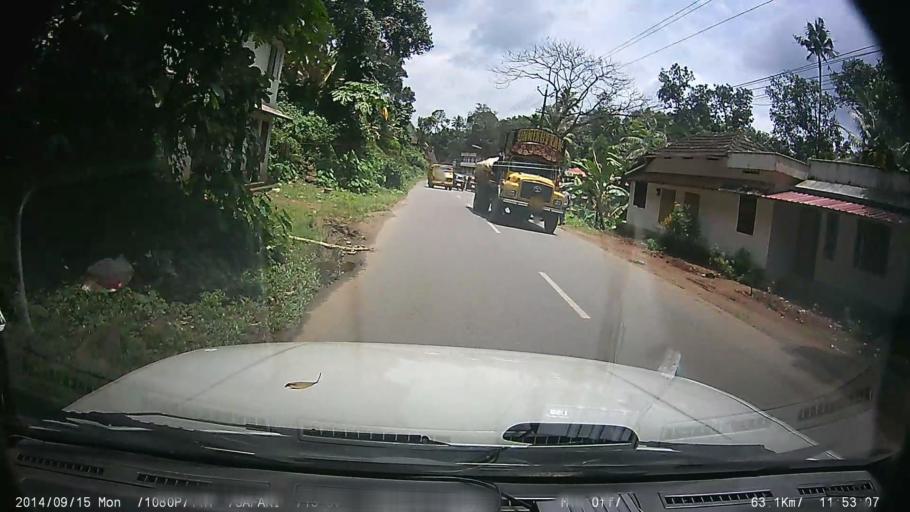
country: IN
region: Kerala
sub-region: Kottayam
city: Palackattumala
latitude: 9.8021
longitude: 76.5747
